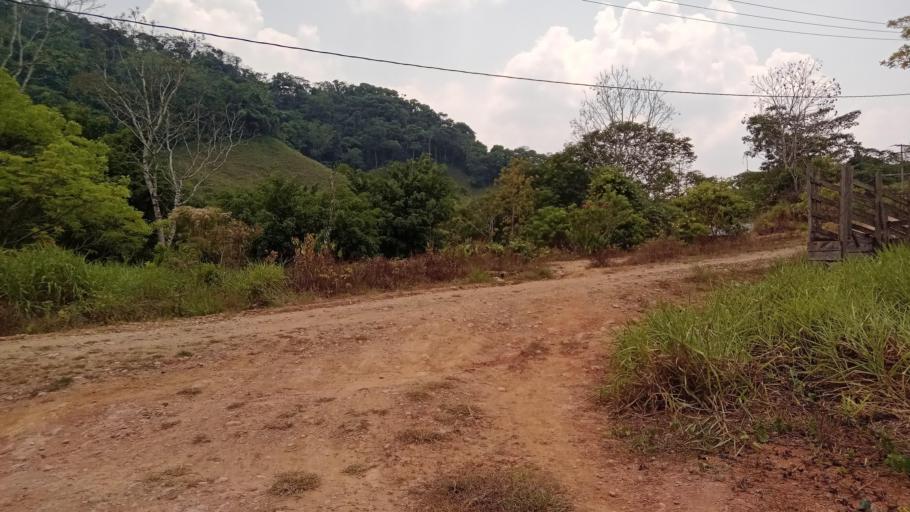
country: MX
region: Tabasco
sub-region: Huimanguillo
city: Francisco Rueda
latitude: 17.5897
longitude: -93.8581
